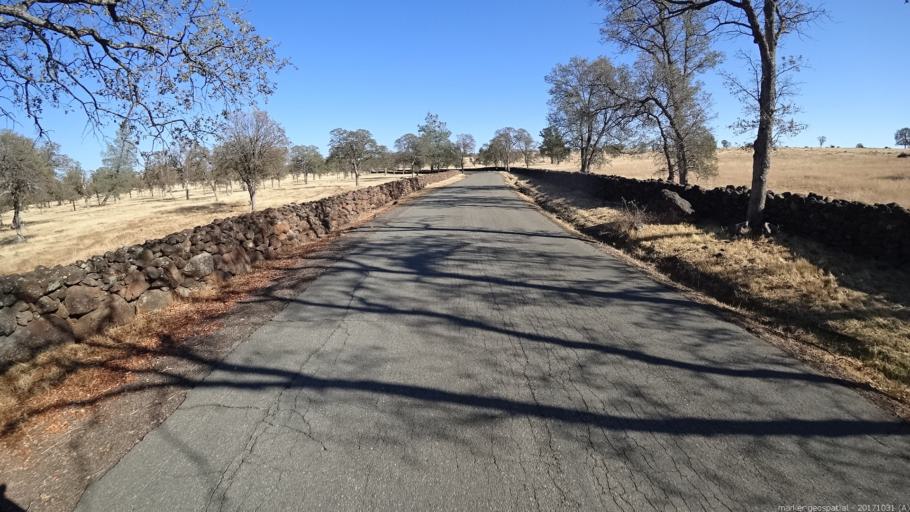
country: US
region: California
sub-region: Shasta County
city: Palo Cedro
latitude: 40.4627
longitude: -122.0843
